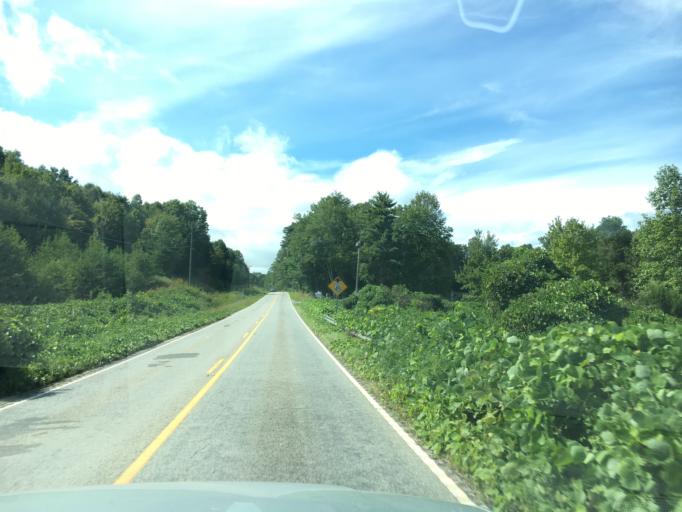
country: US
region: North Carolina
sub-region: Polk County
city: Columbus
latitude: 35.3167
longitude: -82.1742
